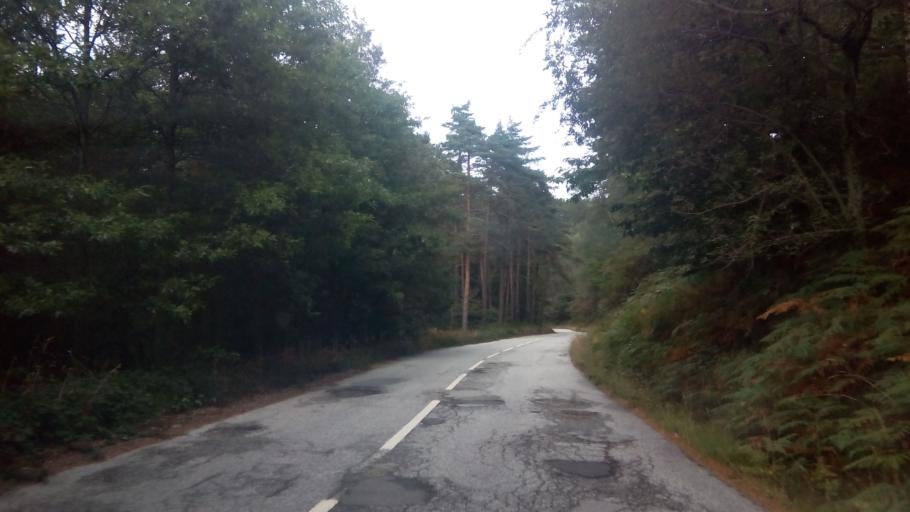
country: PT
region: Vila Real
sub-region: Mesao Frio
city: Mesao Frio
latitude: 41.2773
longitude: -7.9196
